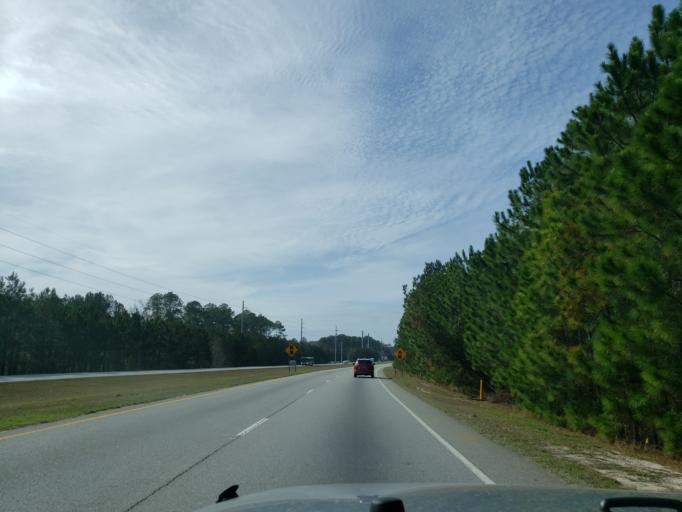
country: US
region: Georgia
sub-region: Chatham County
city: Pooler
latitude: 32.1654
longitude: -81.2277
